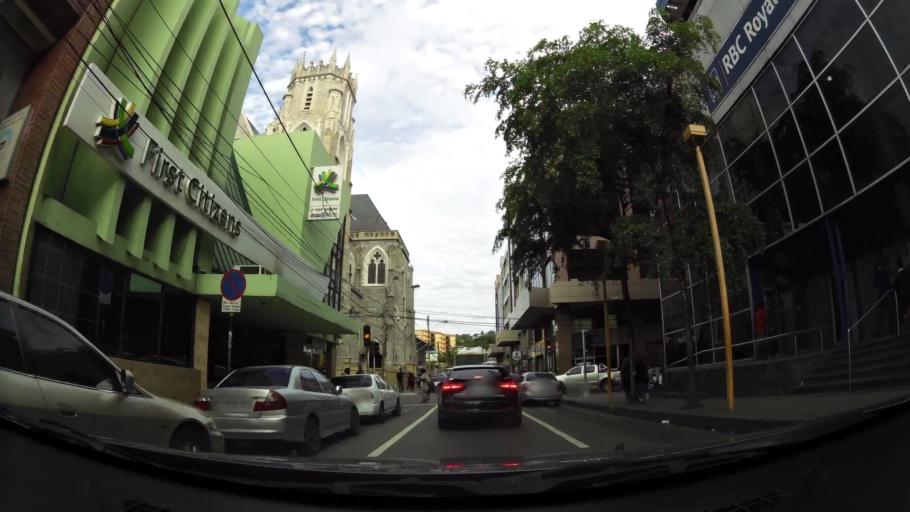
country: TT
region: San Juan/Laventille
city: Laventille
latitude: 10.6567
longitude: -61.5092
